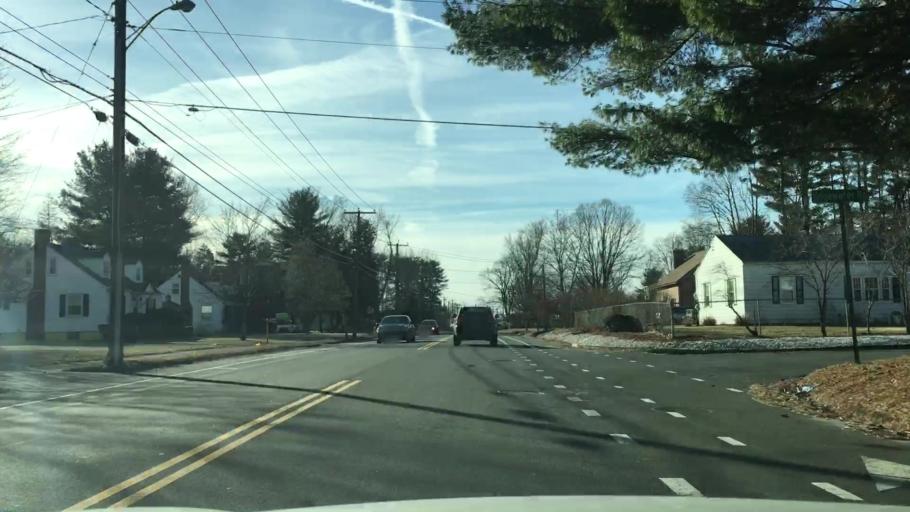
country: US
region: Massachusetts
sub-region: Hampden County
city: Agawam
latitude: 42.0656
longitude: -72.6317
